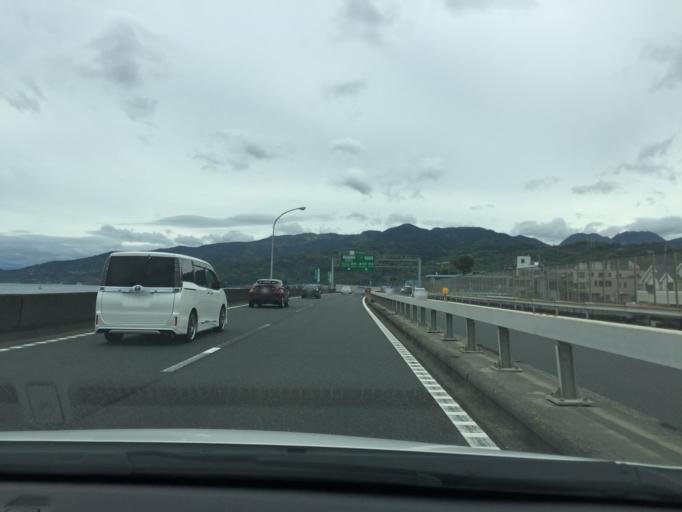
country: JP
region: Kanagawa
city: Odawara
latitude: 35.2467
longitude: 139.1609
